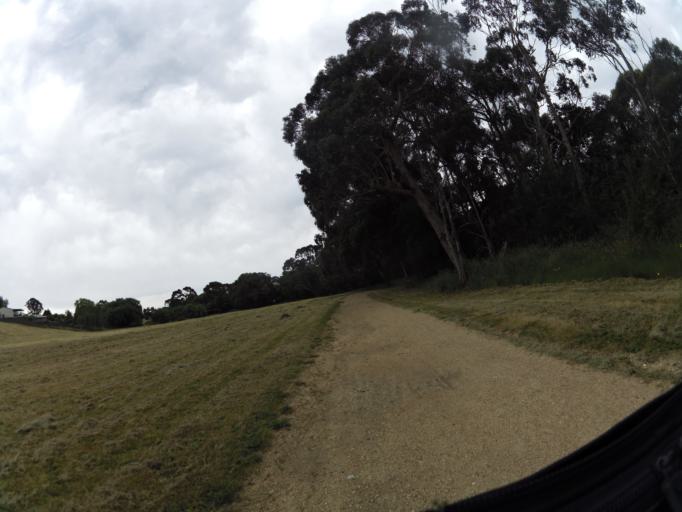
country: AU
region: Victoria
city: Brown Hill
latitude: -37.4311
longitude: 143.9014
